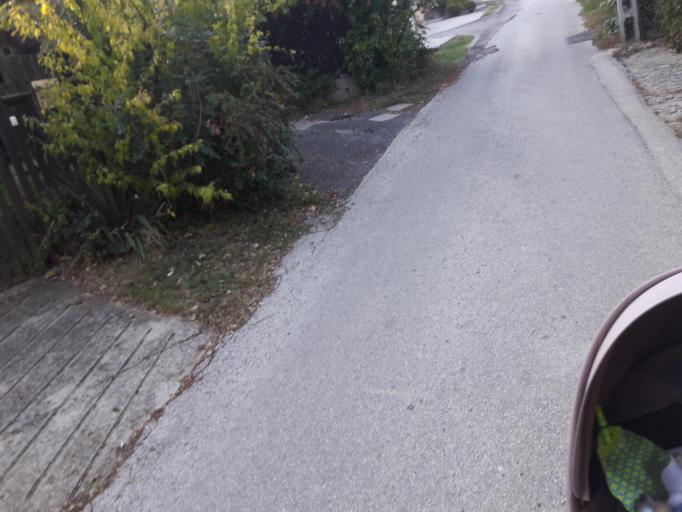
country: HU
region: Pest
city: Budaors
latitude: 47.4777
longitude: 18.9818
